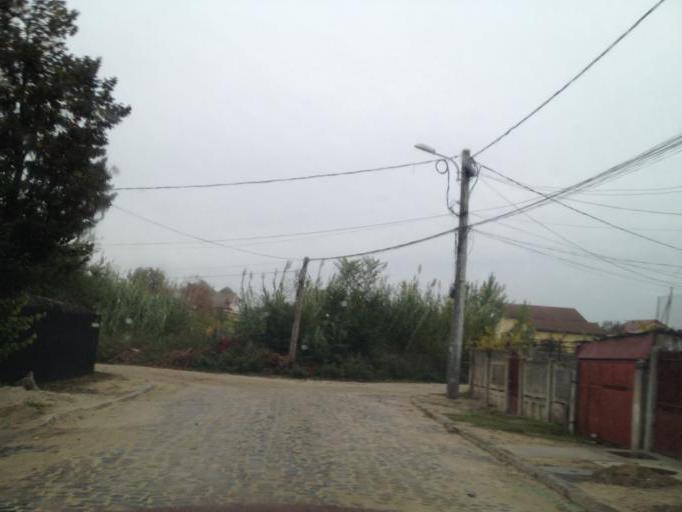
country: RO
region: Dolj
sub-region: Municipiul Craiova
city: Mofleni
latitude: 44.3128
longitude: 23.7759
